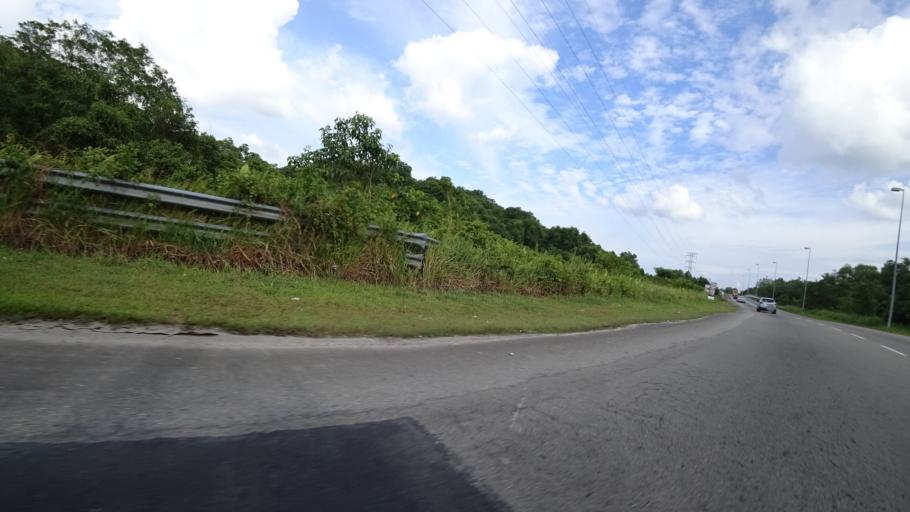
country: BN
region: Brunei and Muara
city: Bandar Seri Begawan
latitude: 4.8207
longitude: 114.8608
